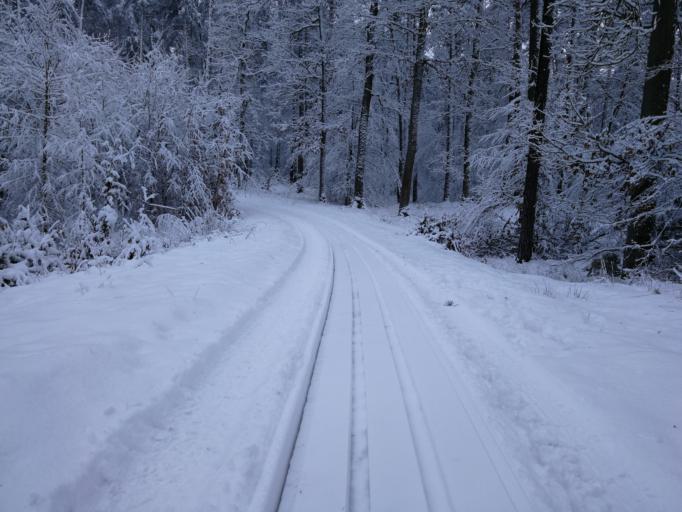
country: PL
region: Kujawsko-Pomorskie
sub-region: Powiat brodnicki
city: Gorzno
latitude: 53.1926
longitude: 19.6782
